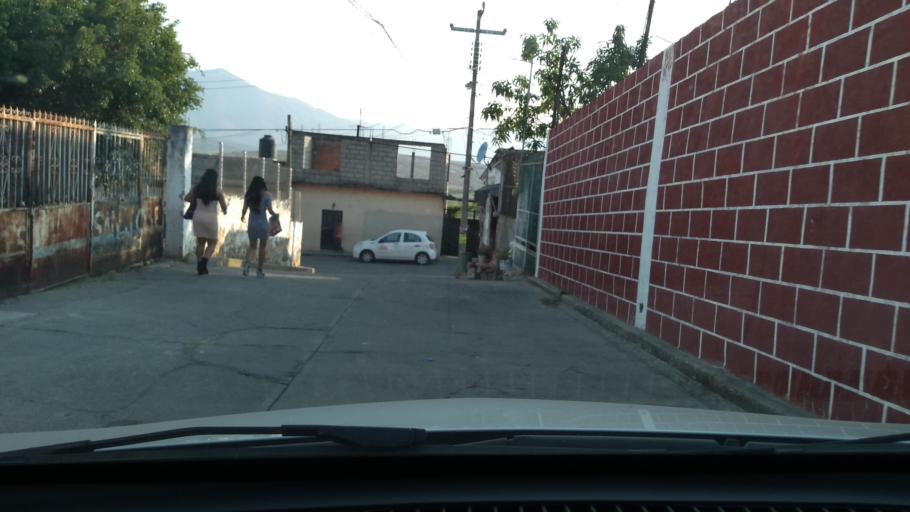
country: MX
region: Morelos
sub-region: Jojutla
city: Tehuixtla
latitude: 18.5618
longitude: -99.2747
